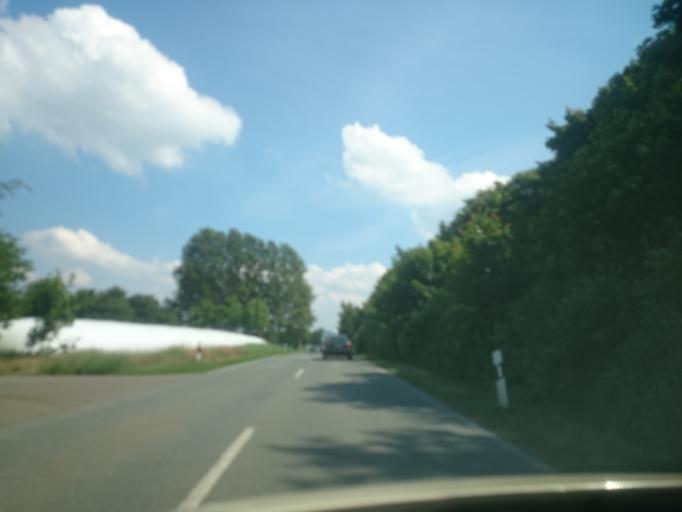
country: DE
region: Saxony
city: Grossolbersdorf
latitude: 50.6802
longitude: 13.1113
